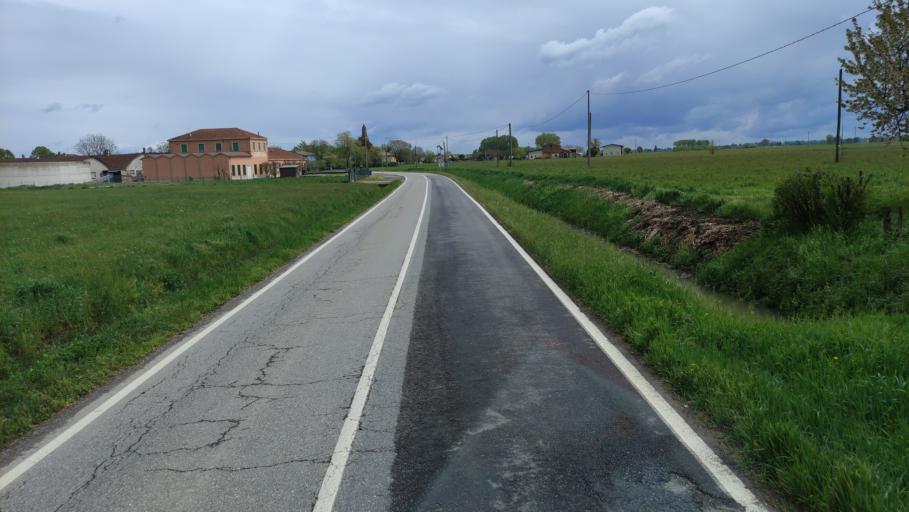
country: IT
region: Emilia-Romagna
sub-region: Provincia di Parma
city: Trecasali
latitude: 44.9533
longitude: 10.2884
